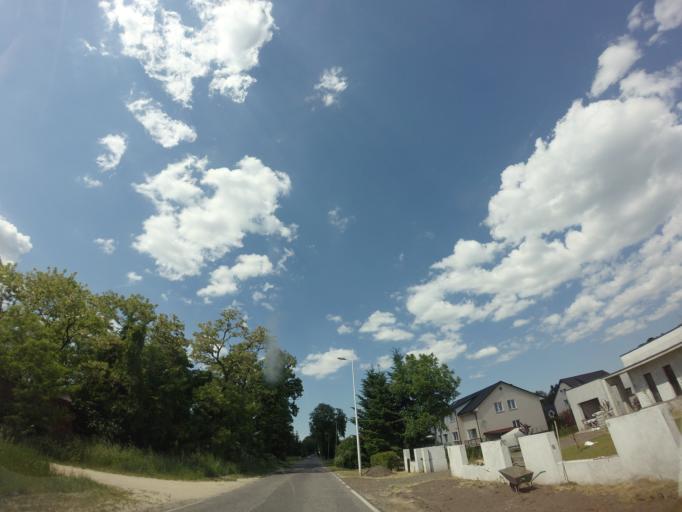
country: PL
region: West Pomeranian Voivodeship
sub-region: Powiat stargardzki
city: Dolice
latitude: 53.1821
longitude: 15.2097
